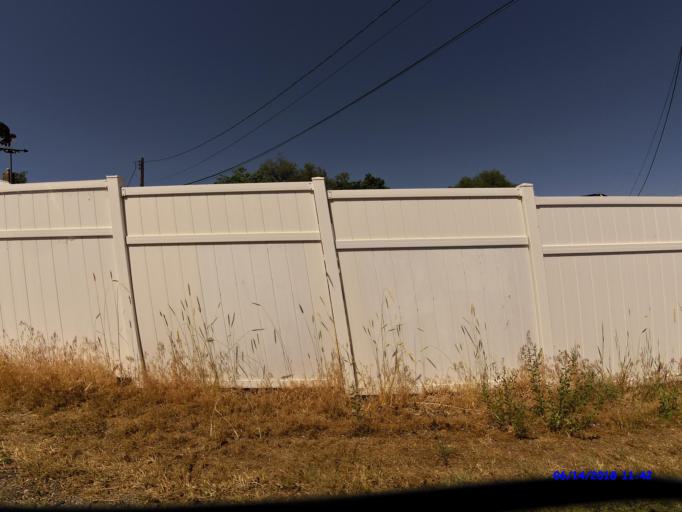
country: US
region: Utah
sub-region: Weber County
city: Ogden
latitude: 41.2217
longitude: -111.9985
